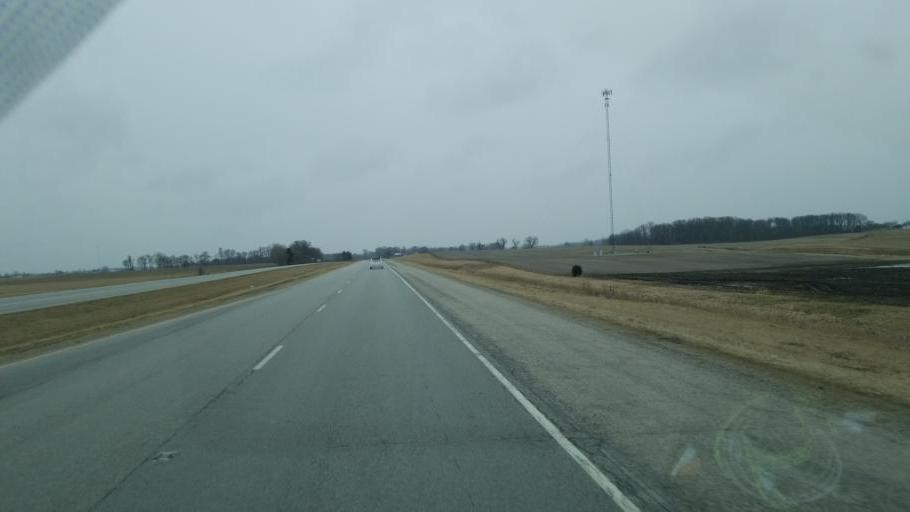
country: US
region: Indiana
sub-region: Fulton County
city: Rochester
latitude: 40.9093
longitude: -86.1595
